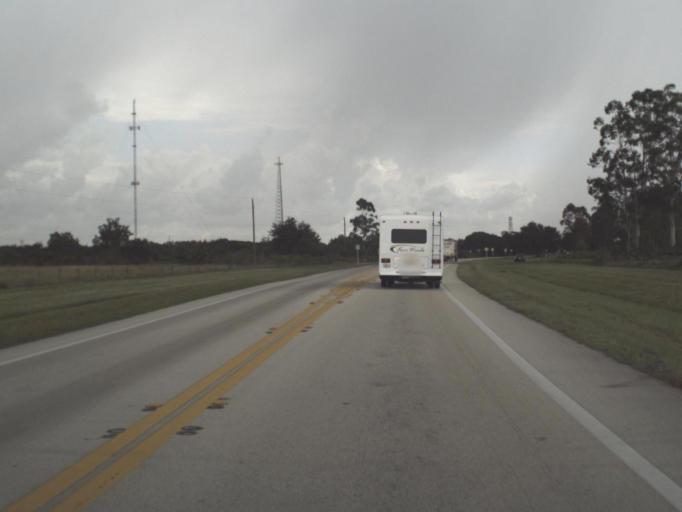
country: US
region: Florida
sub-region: Hendry County
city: Port LaBelle
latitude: 26.9198
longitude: -81.3200
